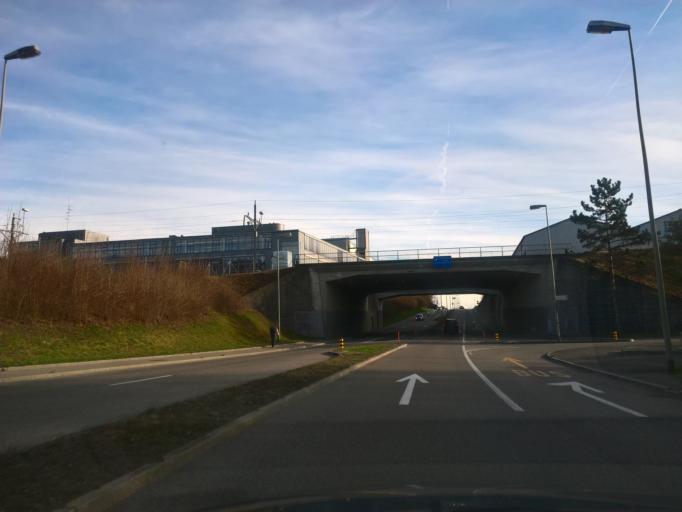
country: CH
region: Zurich
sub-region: Bezirk Buelach
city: Embrach / Kellersacker
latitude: 47.5210
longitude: 8.5942
